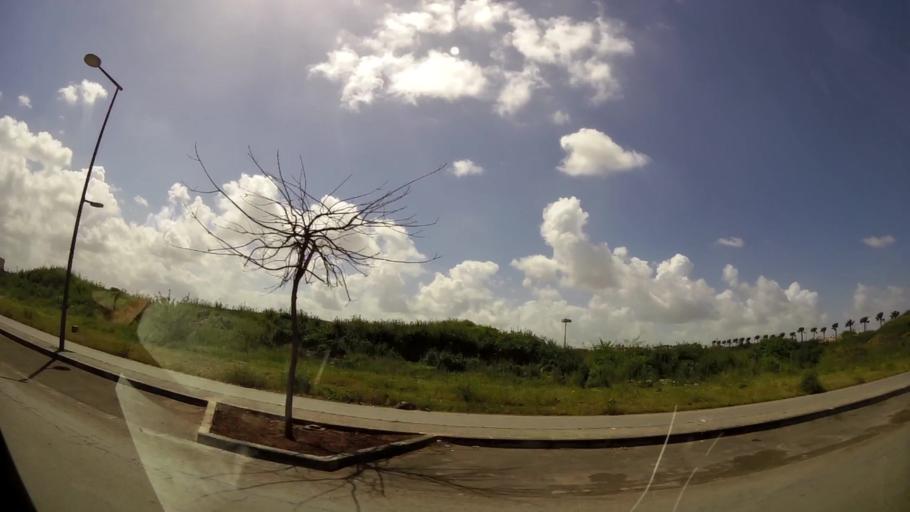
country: MA
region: Grand Casablanca
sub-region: Mediouna
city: Tit Mellil
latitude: 33.6336
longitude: -7.4612
